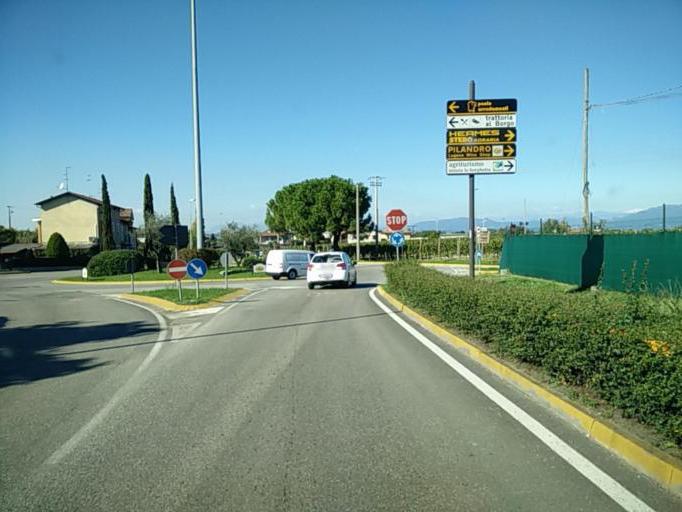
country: IT
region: Lombardy
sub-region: Provincia di Brescia
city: San Martino della Battaglia
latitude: 45.4422
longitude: 10.5992
